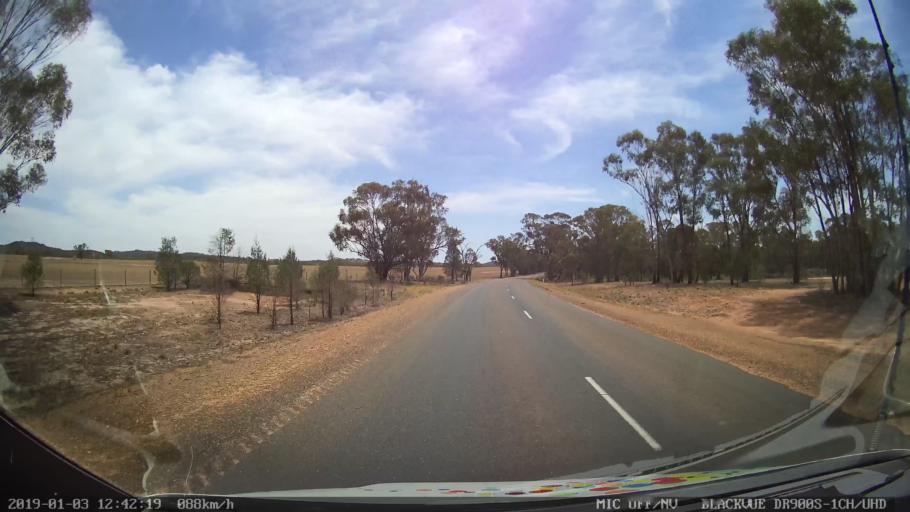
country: AU
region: New South Wales
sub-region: Weddin
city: Grenfell
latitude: -33.7888
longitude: 148.2115
